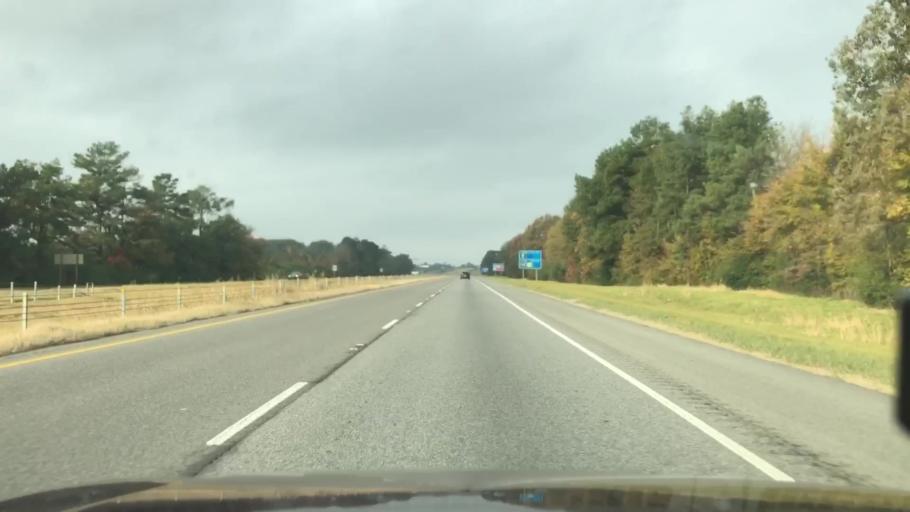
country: US
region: Louisiana
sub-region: Richland Parish
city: Rayville
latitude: 32.4567
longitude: -91.7459
